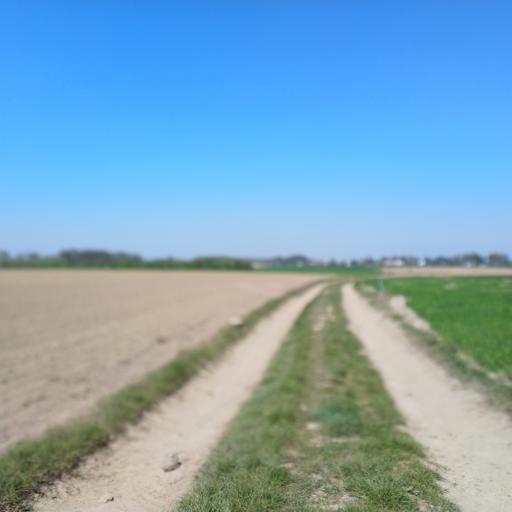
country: BE
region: Wallonia
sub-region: Province du Hainaut
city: Jurbise
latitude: 50.5369
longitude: 3.9036
